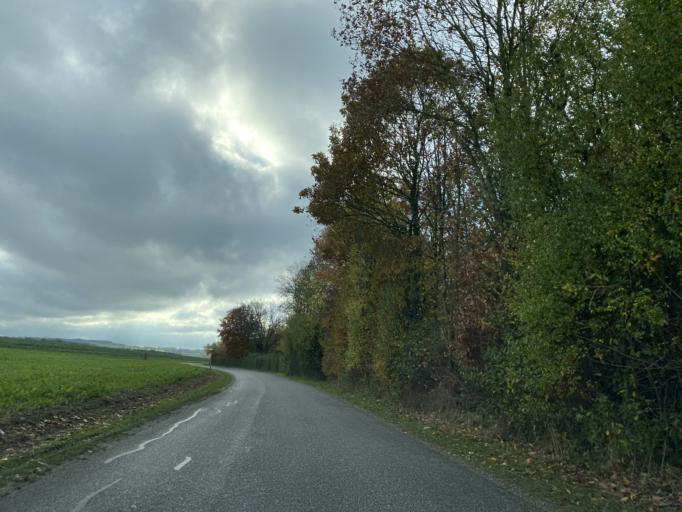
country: DK
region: Central Jutland
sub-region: Favrskov Kommune
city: Hammel
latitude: 56.2515
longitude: 9.7759
